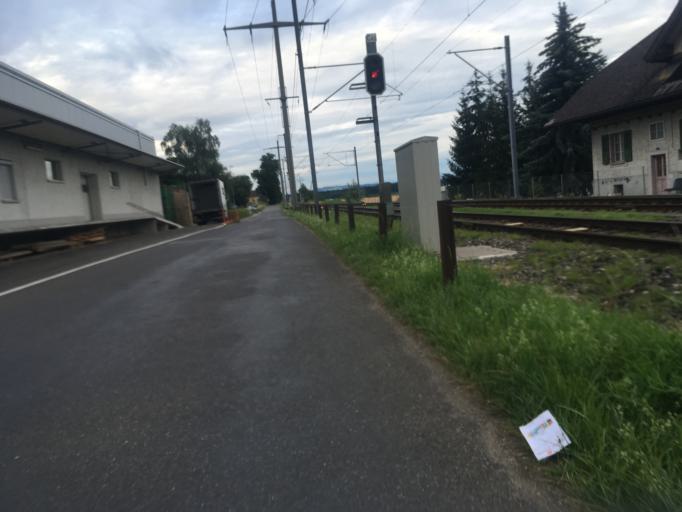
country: CH
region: Bern
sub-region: Seeland District
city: Ins
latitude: 46.9985
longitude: 7.1055
